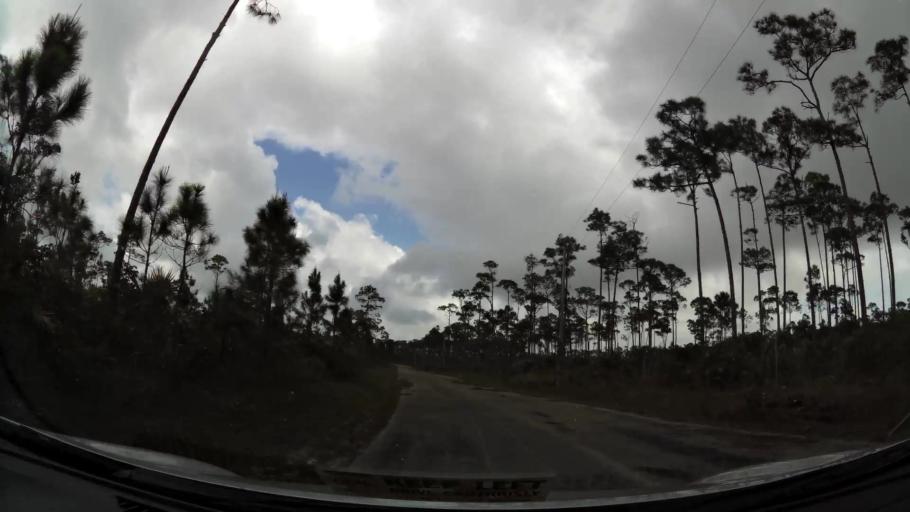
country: BS
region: Freeport
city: Lucaya
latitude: 26.5580
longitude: -78.5767
